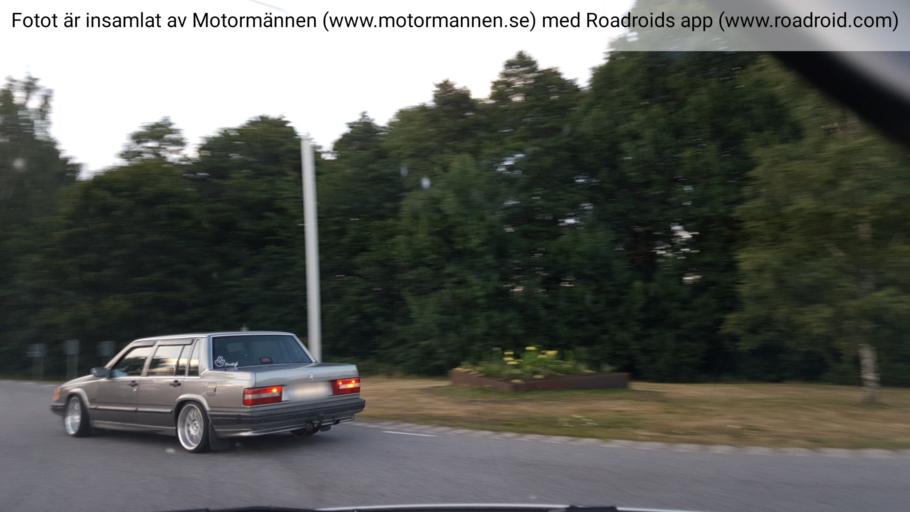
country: SE
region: Vaestra Goetaland
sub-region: Tibro Kommun
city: Tibro
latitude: 58.4098
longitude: 14.1815
